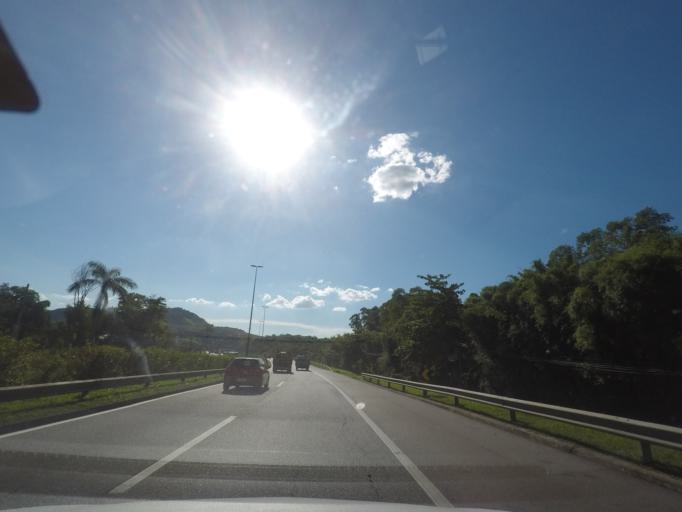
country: BR
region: Rio de Janeiro
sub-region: Petropolis
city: Petropolis
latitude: -22.6558
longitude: -43.1236
